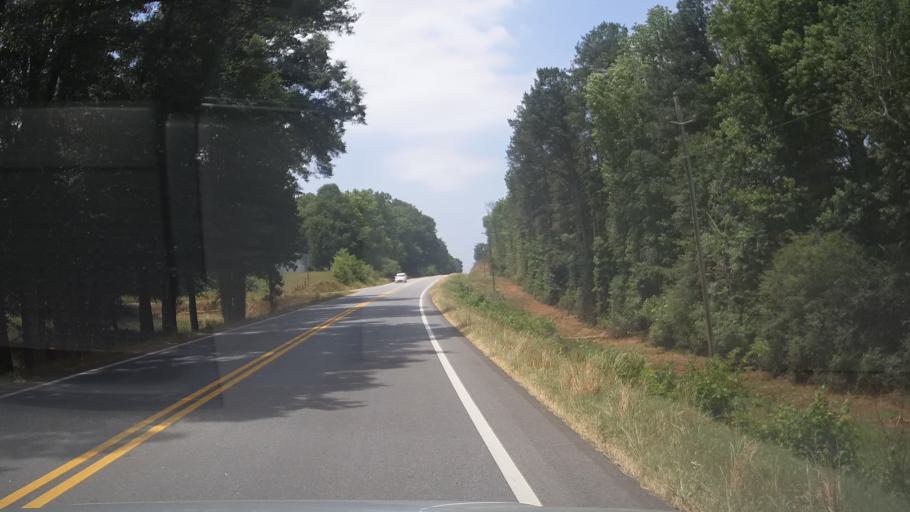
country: US
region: Georgia
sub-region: Madison County
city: Danielsville
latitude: 34.1761
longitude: -83.3148
